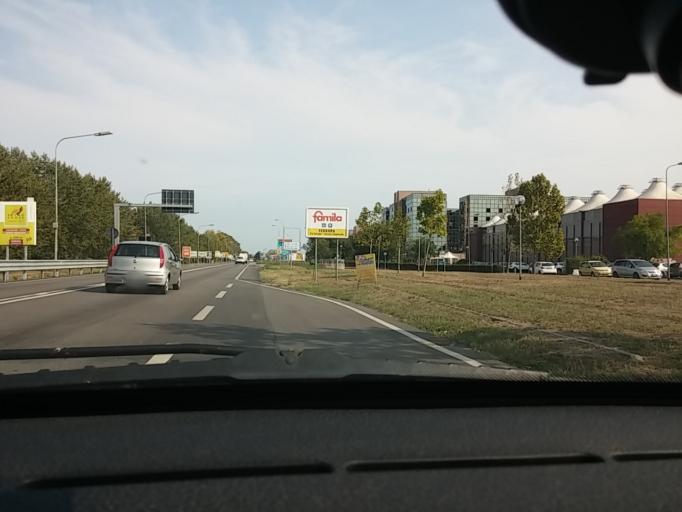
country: IT
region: Emilia-Romagna
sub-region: Provincia di Ferrara
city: Ferrara
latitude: 44.8227
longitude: 11.5934
